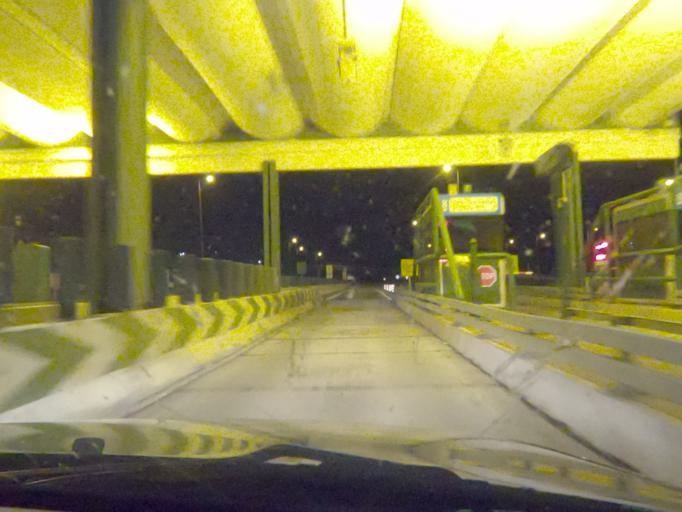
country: PT
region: Evora
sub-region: Estremoz
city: Estremoz
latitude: 38.8236
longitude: -7.6084
